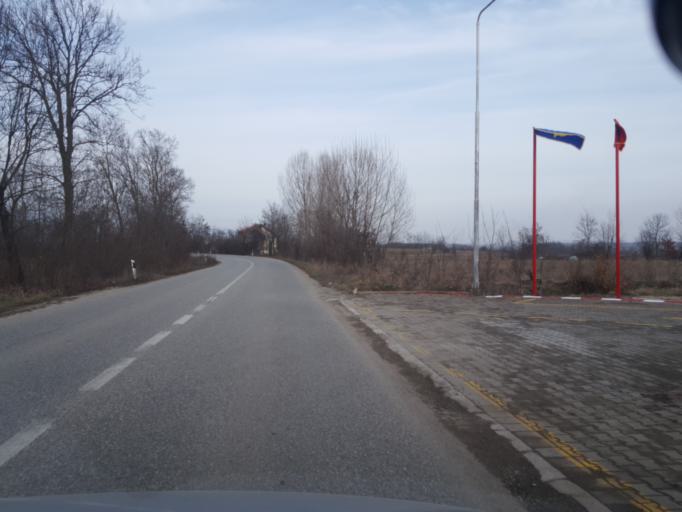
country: XK
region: Pec
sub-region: Komuna e Istogut
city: Istok
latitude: 42.7389
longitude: 20.4809
